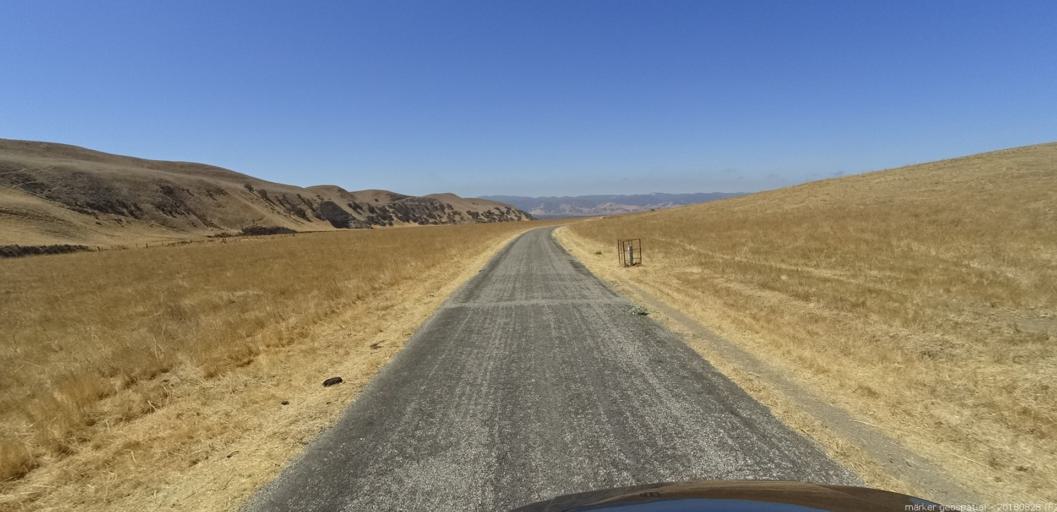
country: US
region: California
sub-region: San Luis Obispo County
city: Lake Nacimiento
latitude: 36.0346
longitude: -120.8481
